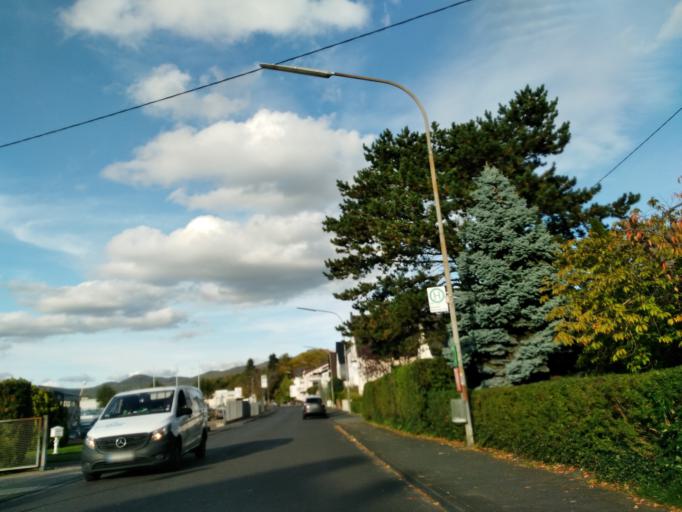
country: DE
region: Rheinland-Pfalz
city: Rheinbreitbach
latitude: 50.6228
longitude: 7.2291
